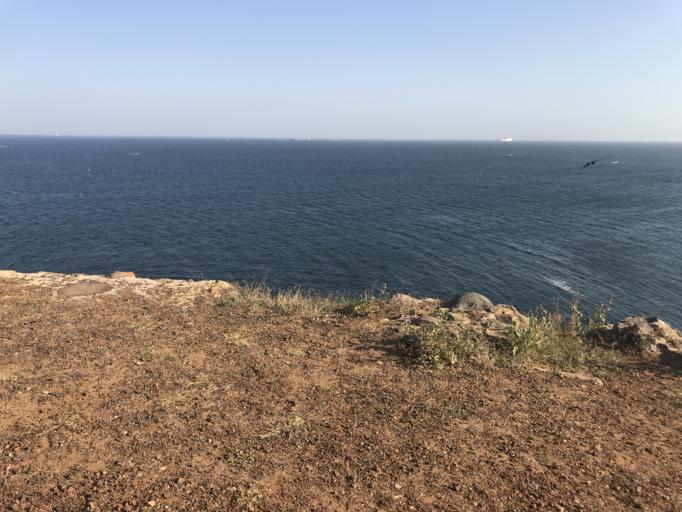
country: SN
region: Dakar
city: Dakar
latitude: 14.6639
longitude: -17.3982
